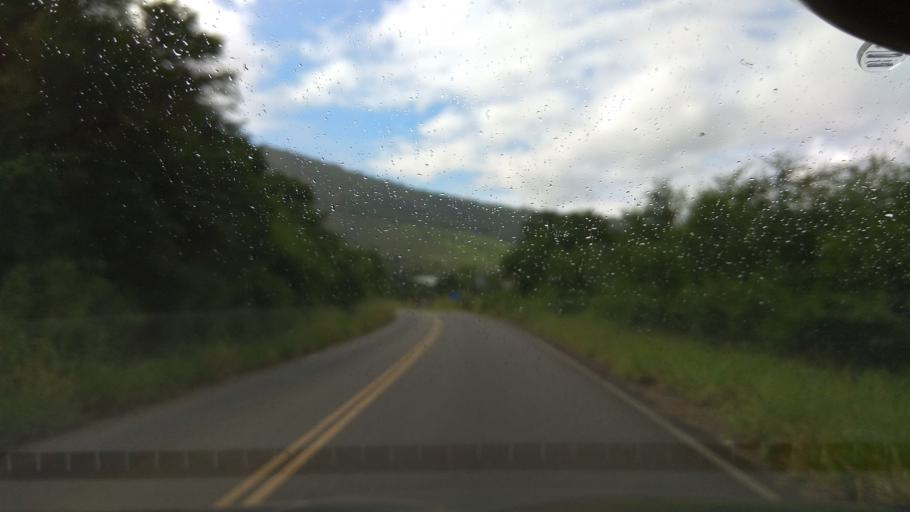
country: BR
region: Bahia
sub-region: Ubaira
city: Ubaira
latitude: -13.2510
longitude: -39.7190
